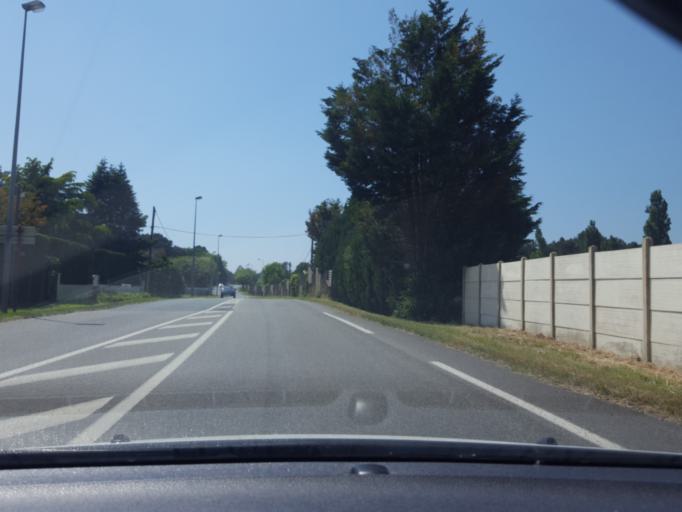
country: FR
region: Aquitaine
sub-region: Departement des Landes
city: Tarnos
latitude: 43.5526
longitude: -1.4621
